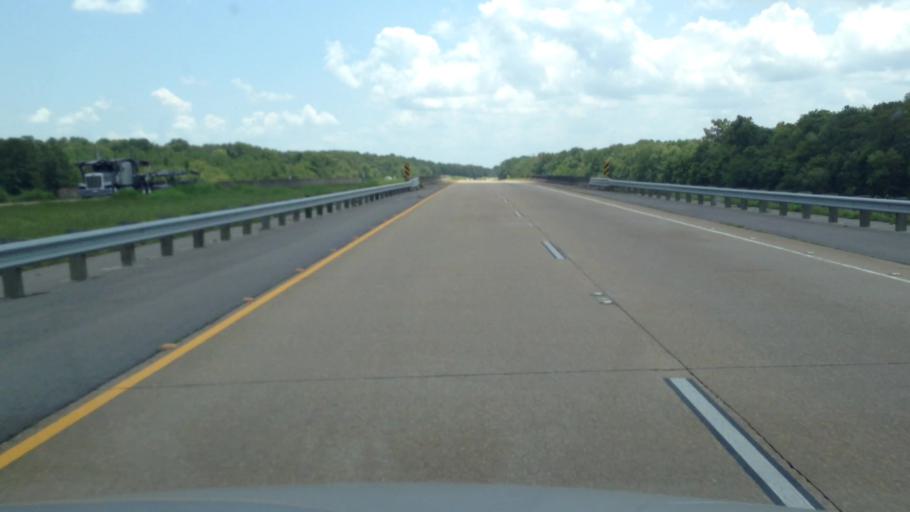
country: US
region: Louisiana
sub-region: Rapides Parish
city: Woodworth
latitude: 31.1652
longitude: -92.4603
